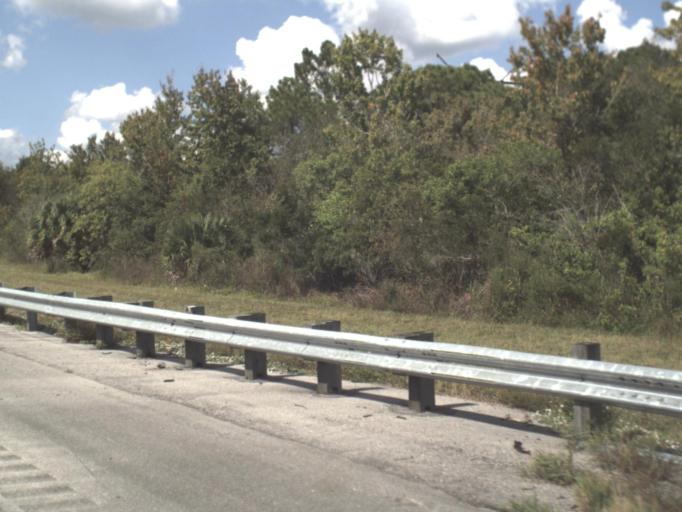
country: US
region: Florida
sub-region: Indian River County
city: Fellsmere
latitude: 27.5605
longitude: -80.7722
